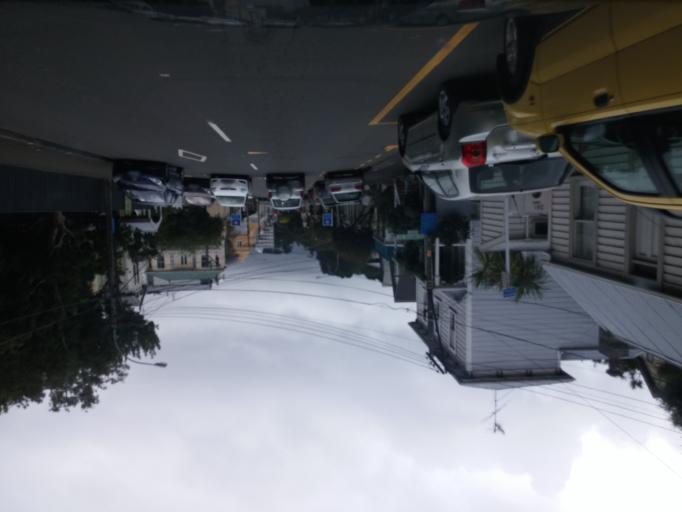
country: NZ
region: Wellington
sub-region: Wellington City
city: Kelburn
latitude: -41.2771
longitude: 174.7712
